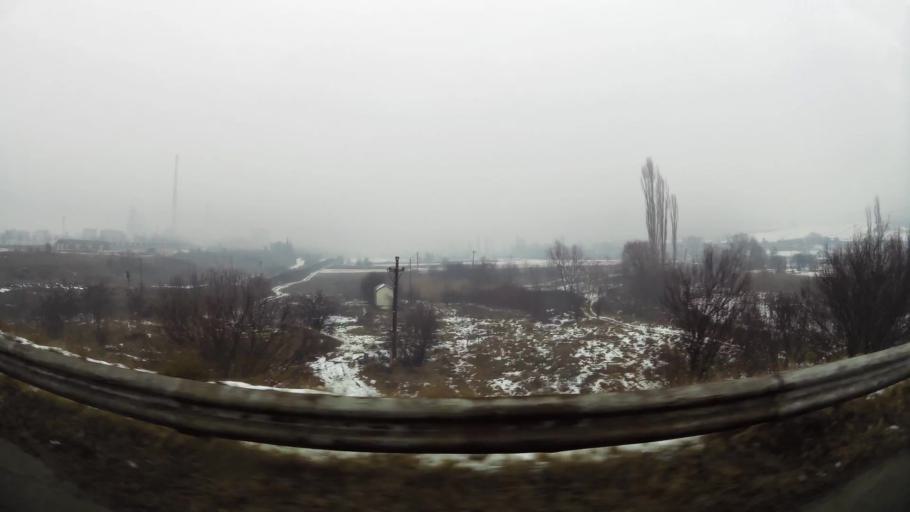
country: MK
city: Miladinovci
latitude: 41.9985
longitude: 21.6597
